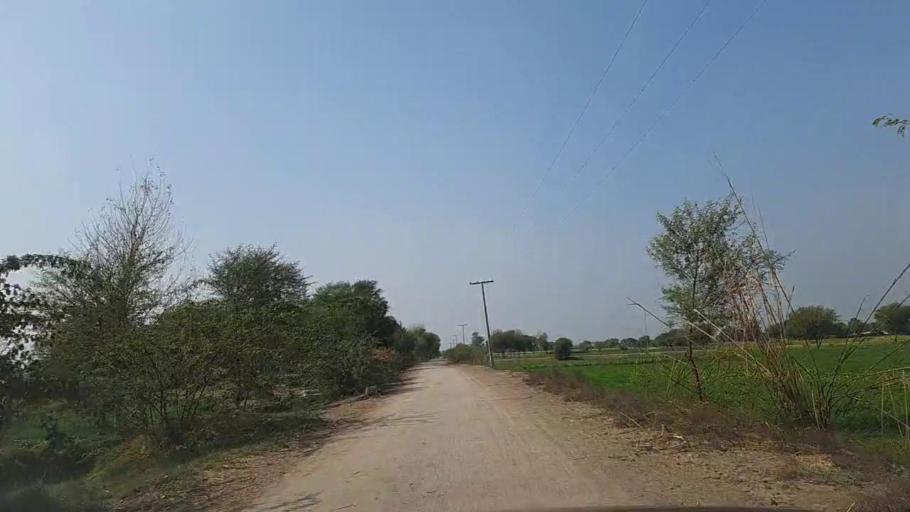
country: PK
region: Sindh
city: Nawabshah
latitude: 26.2475
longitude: 68.4824
